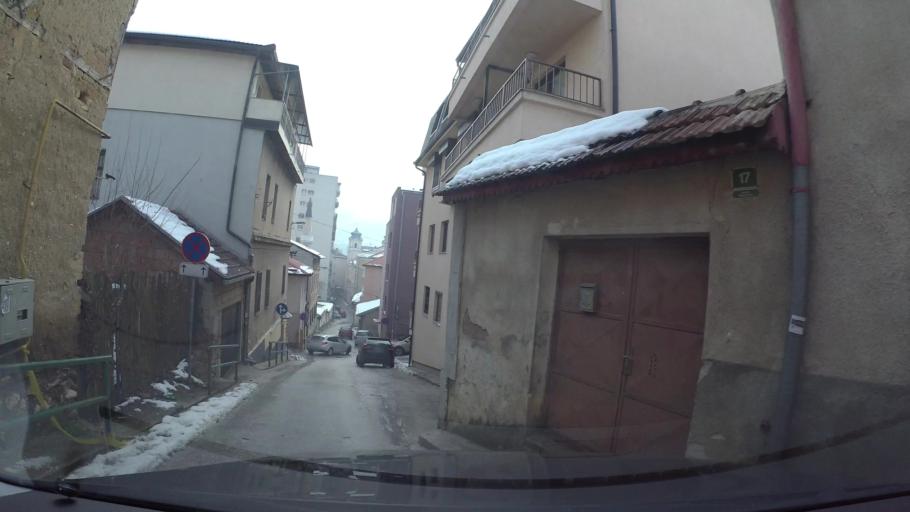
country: BA
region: Federation of Bosnia and Herzegovina
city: Kobilja Glava
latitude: 43.8624
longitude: 18.4227
